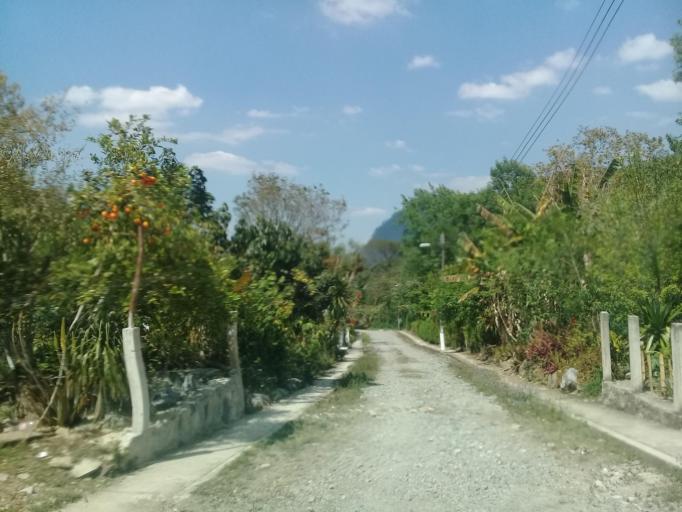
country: MX
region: Veracruz
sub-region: Tlilapan
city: Tonalixco
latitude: 18.8029
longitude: -97.0729
